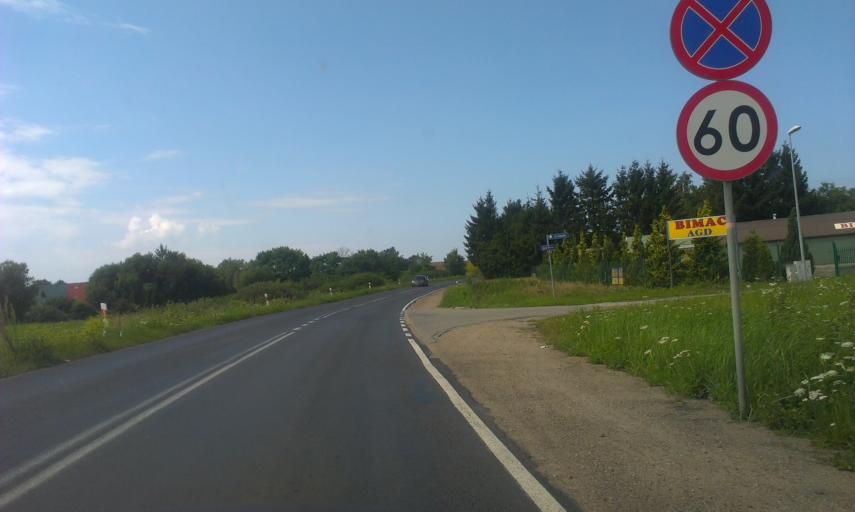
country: PL
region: West Pomeranian Voivodeship
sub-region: Powiat kolobrzeski
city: Kolobrzeg
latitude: 54.1556
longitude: 15.6107
